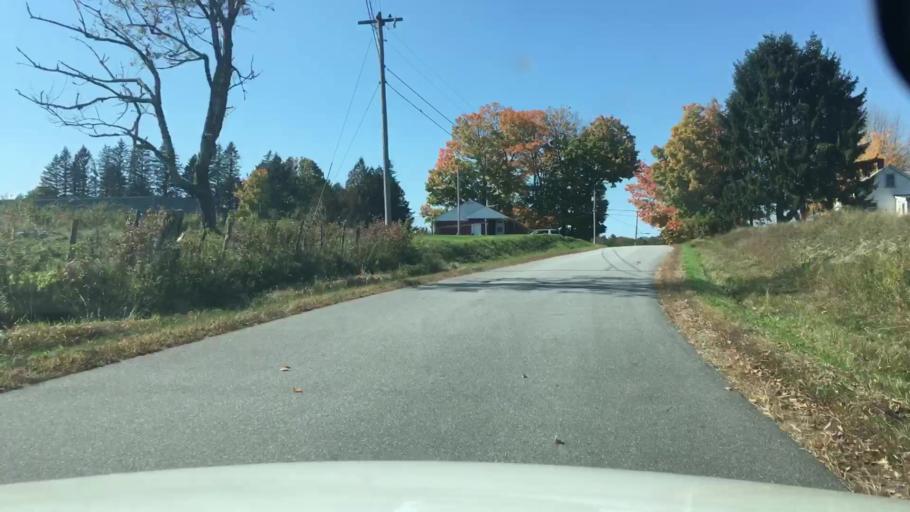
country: US
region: Maine
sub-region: Sagadahoc County
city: Topsham
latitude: 44.0134
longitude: -69.9683
